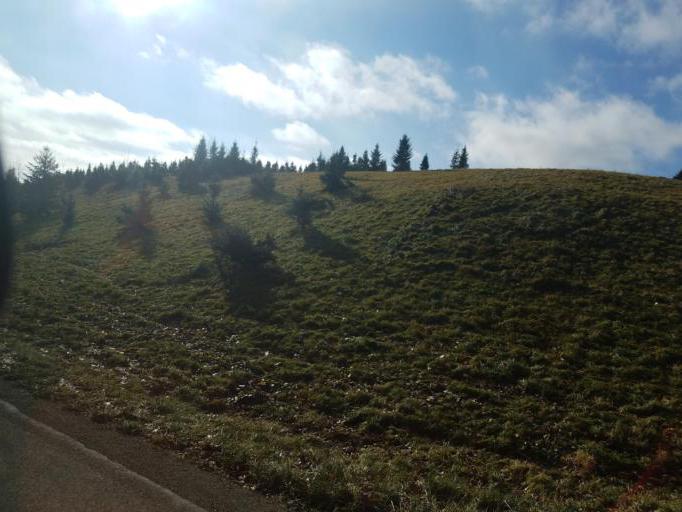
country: US
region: Ohio
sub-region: Sandusky County
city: Bellville
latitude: 40.5782
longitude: -82.4758
